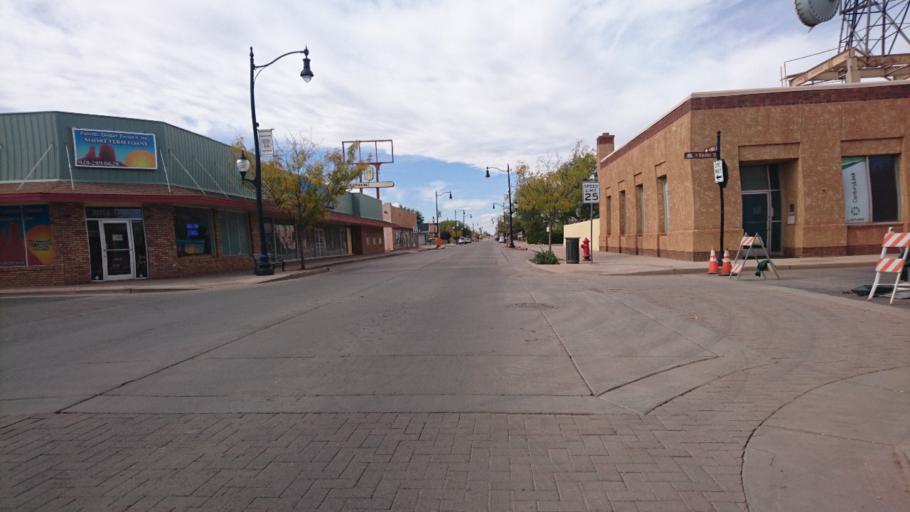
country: US
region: Arizona
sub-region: Navajo County
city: Winslow
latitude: 35.0242
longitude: -110.6974
